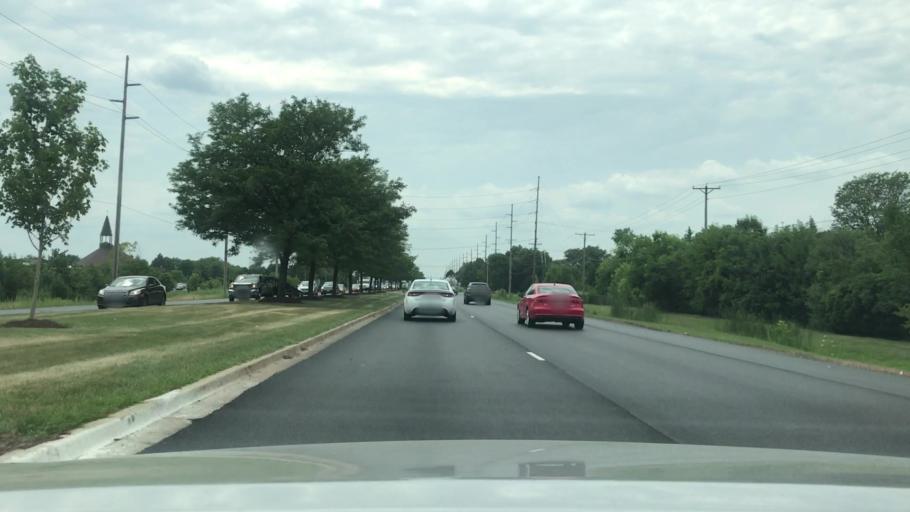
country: US
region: Illinois
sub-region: DuPage County
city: Naperville
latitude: 41.7479
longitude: -88.1552
